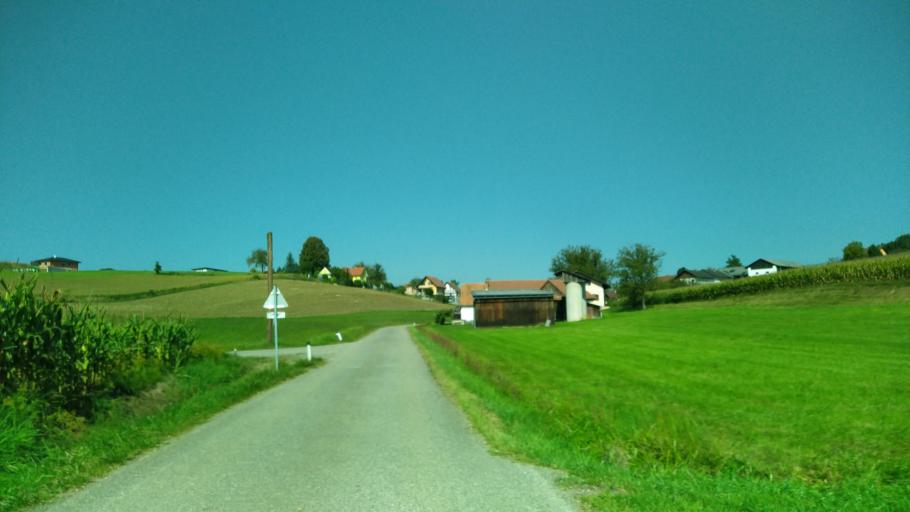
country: AT
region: Styria
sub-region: Politischer Bezirk Deutschlandsberg
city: Wettmannstatten
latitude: 46.8201
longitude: 15.3735
